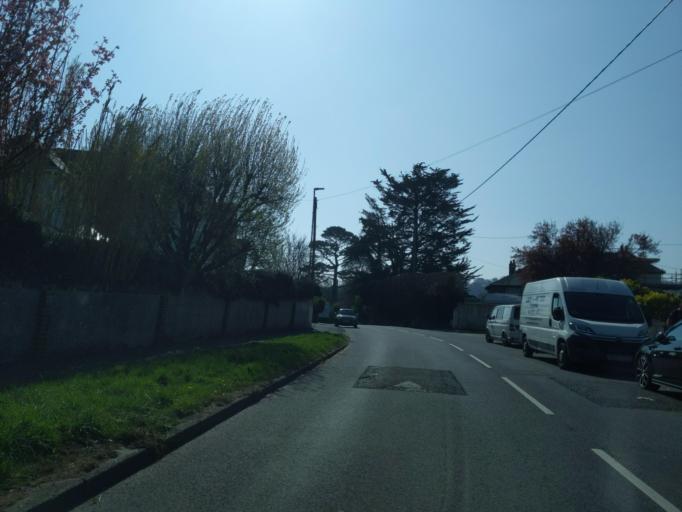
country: GB
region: England
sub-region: Devon
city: Plympton
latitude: 50.3940
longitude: -4.0617
